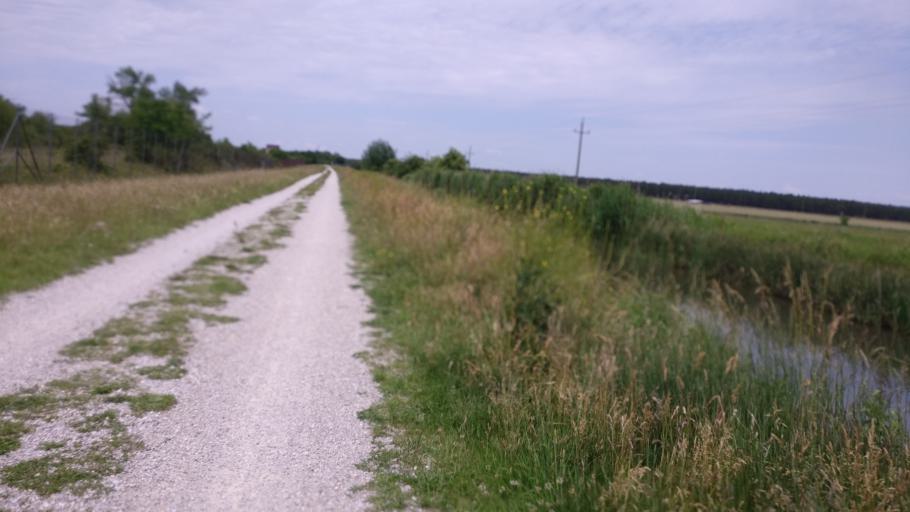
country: AT
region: Lower Austria
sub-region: Politischer Bezirk Wiener Neustadt
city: Lichtenworth
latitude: 47.8533
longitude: 16.2794
